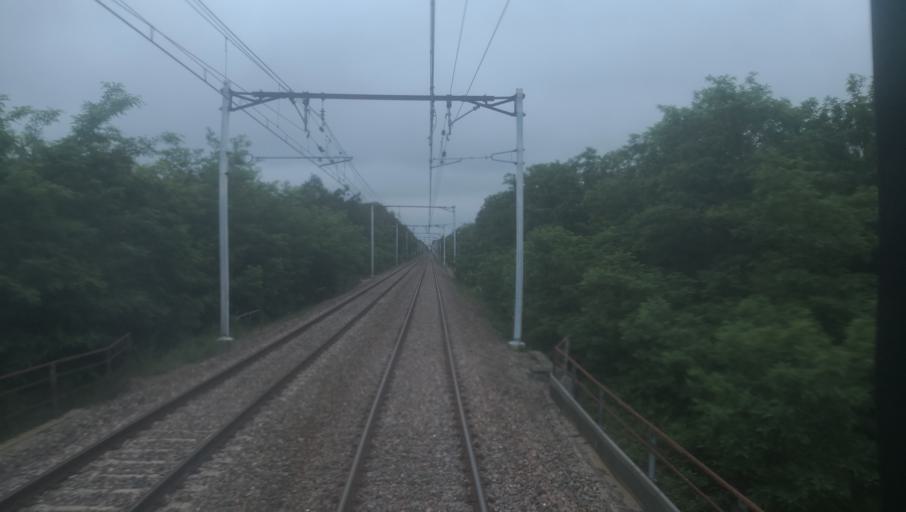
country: FR
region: Centre
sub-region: Departement du Loir-et-Cher
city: Theillay
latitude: 47.3391
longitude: 2.0463
